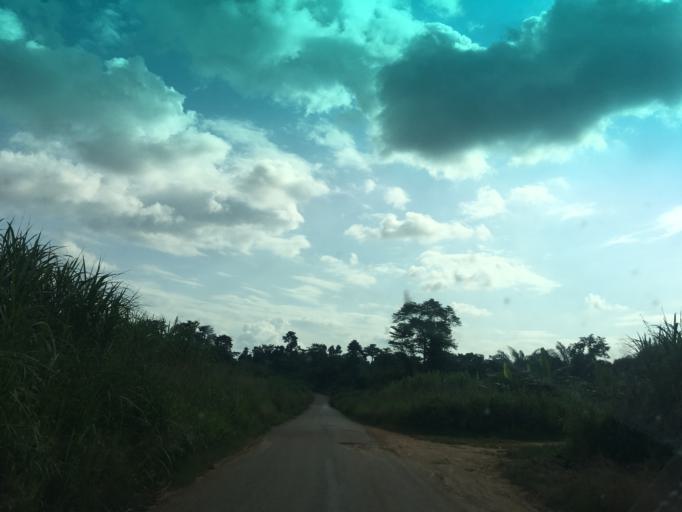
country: GH
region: Western
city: Bibiani
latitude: 6.7822
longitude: -2.5495
